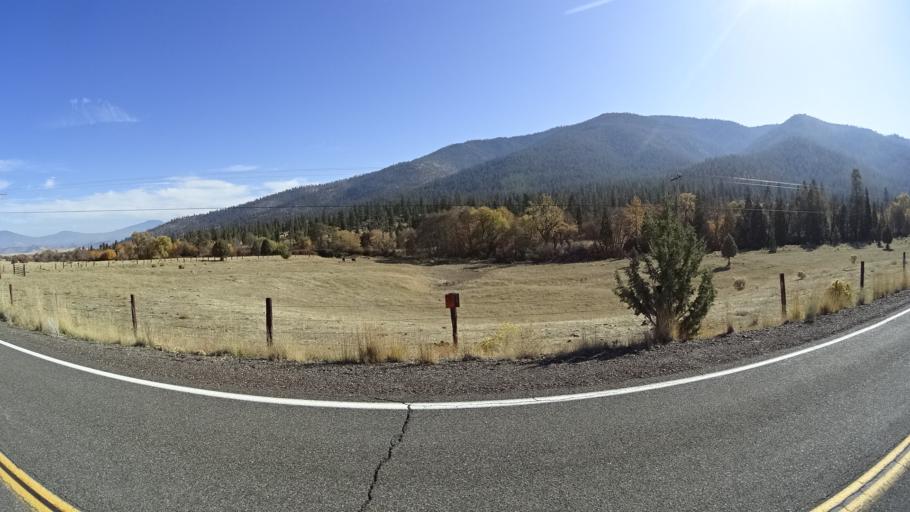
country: US
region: California
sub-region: Siskiyou County
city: Weed
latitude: 41.4839
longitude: -122.5713
